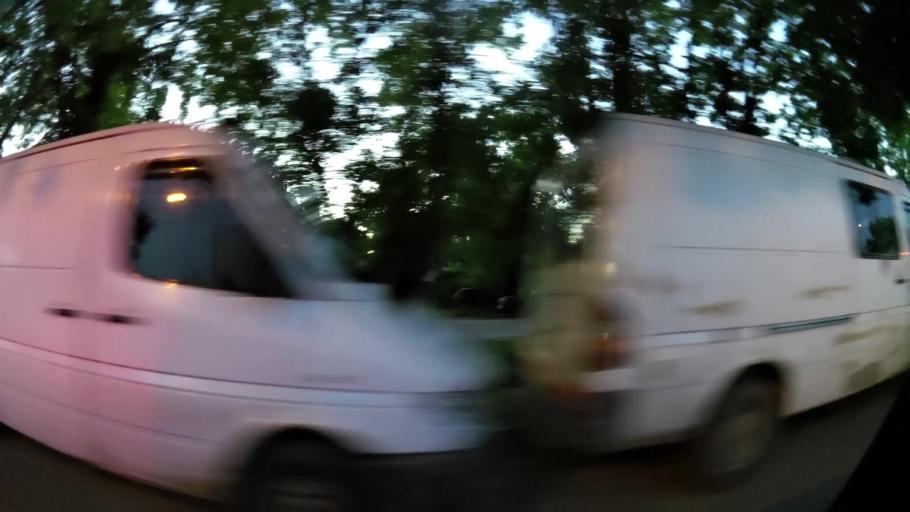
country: AR
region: Buenos Aires
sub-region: Partido de Almirante Brown
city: Adrogue
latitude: -34.7808
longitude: -58.3240
